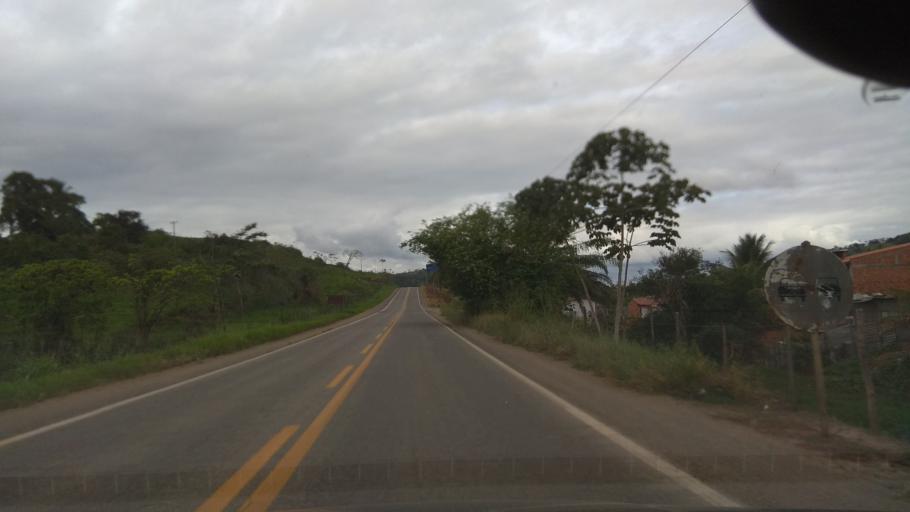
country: BR
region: Bahia
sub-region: Ipiau
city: Ipiau
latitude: -14.1439
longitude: -39.7174
